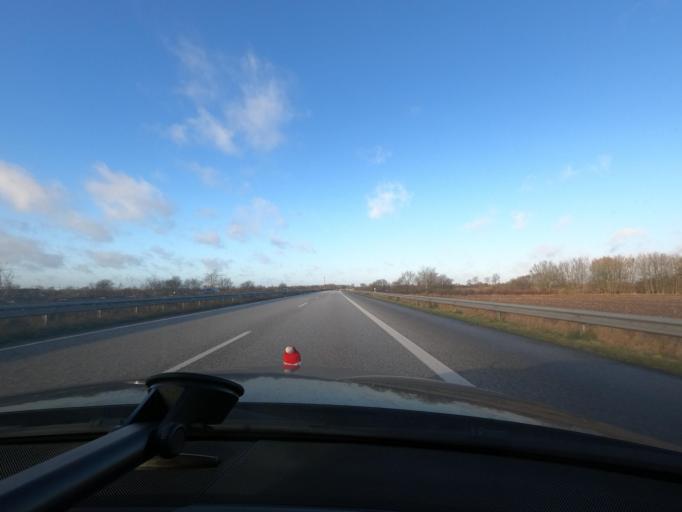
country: DE
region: Schleswig-Holstein
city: Oeversee
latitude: 54.6921
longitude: 9.4094
